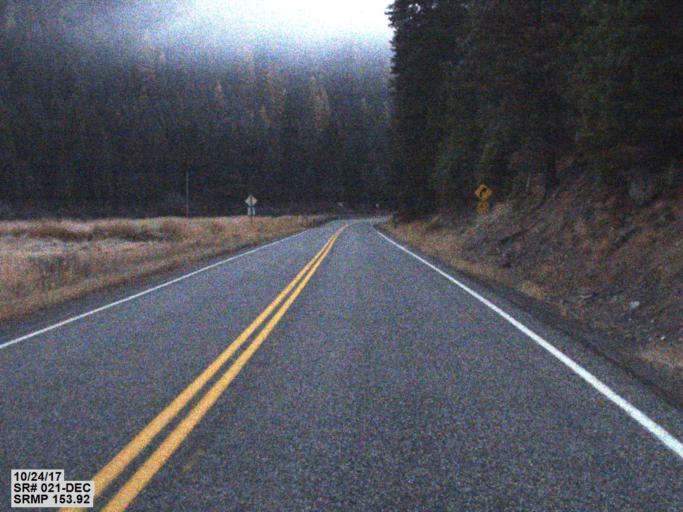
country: US
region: Washington
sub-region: Ferry County
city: Republic
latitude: 48.5561
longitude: -118.7445
